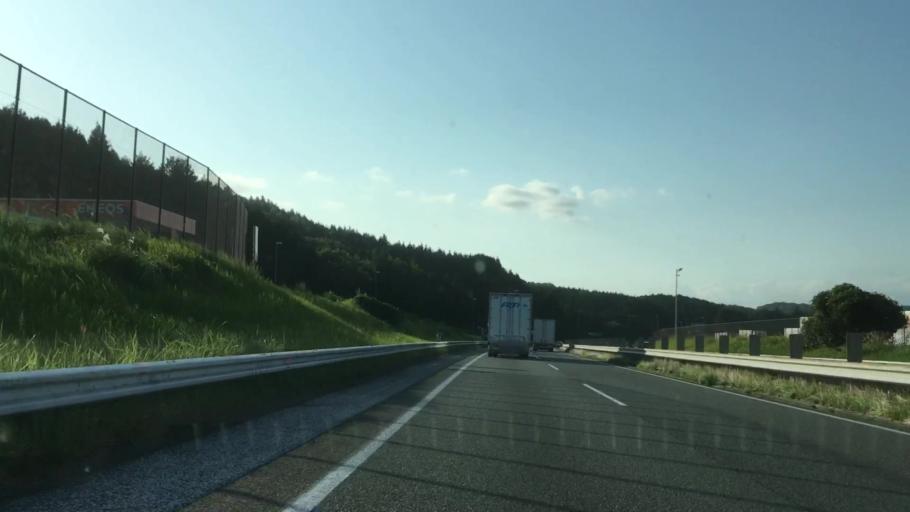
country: JP
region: Yamaguchi
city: Ogori-shimogo
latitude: 34.1534
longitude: 131.3377
